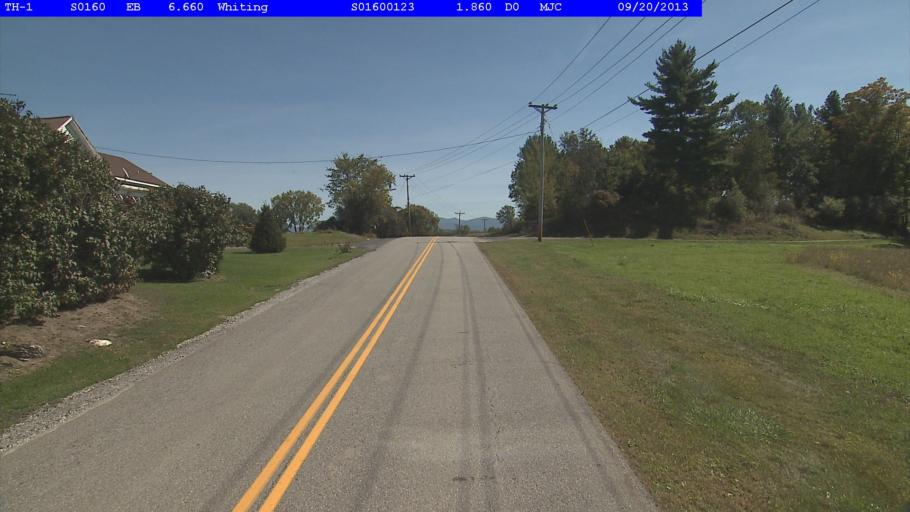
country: US
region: Vermont
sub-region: Rutland County
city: Brandon
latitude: 43.8606
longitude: -73.1895
